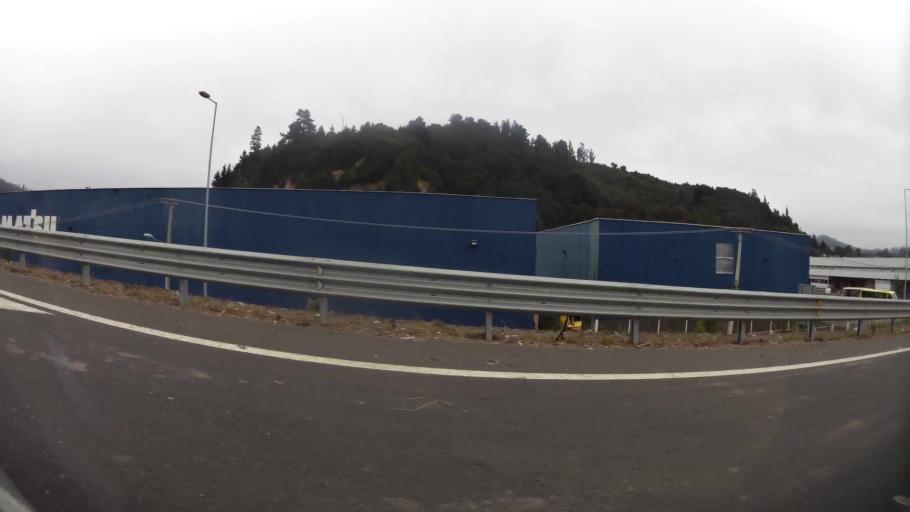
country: CL
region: Biobio
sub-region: Provincia de Concepcion
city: Concepcion
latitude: -36.8211
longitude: -72.9976
